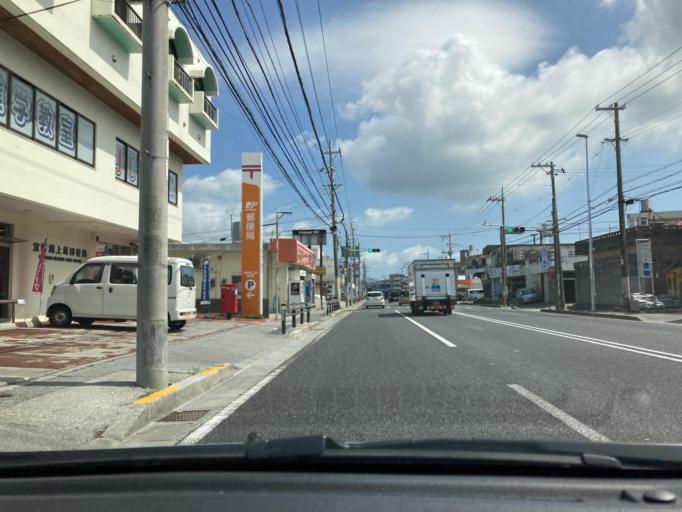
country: JP
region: Okinawa
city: Ginowan
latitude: 26.2754
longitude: 127.7750
